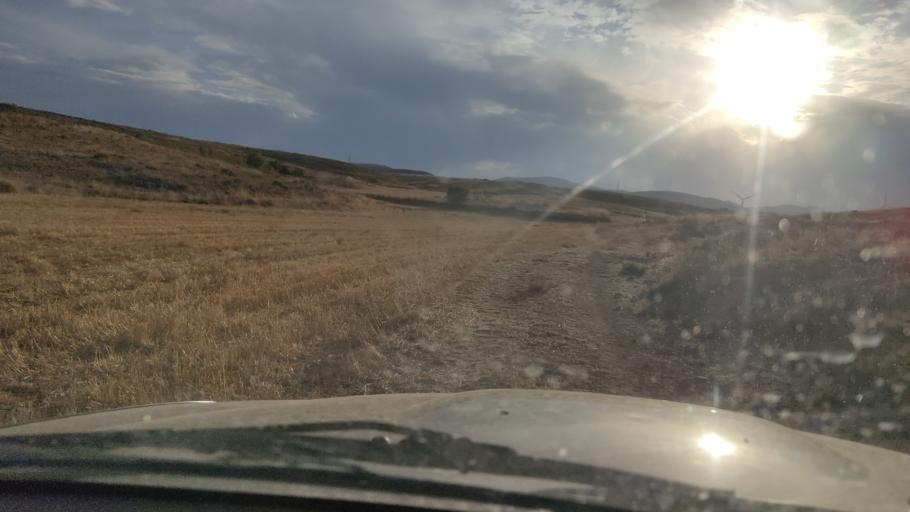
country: ES
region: Aragon
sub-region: Provincia de Teruel
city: Monforte de Moyuela
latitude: 41.0715
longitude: -0.9937
